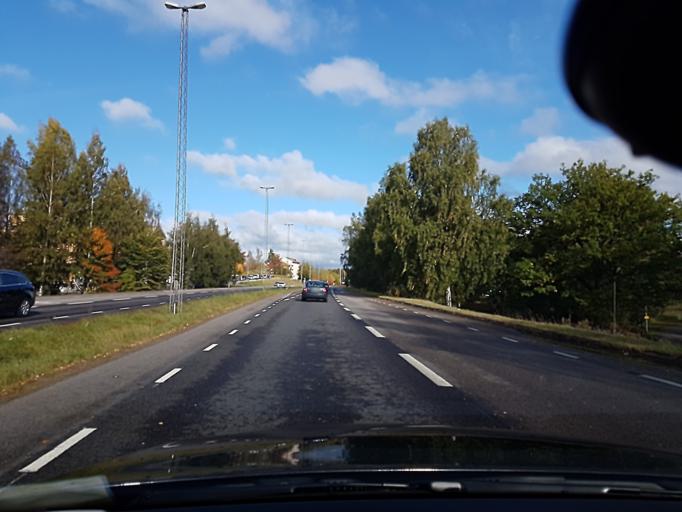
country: SE
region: Kronoberg
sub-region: Vaxjo Kommun
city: Vaexjoe
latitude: 56.8635
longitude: 14.8195
